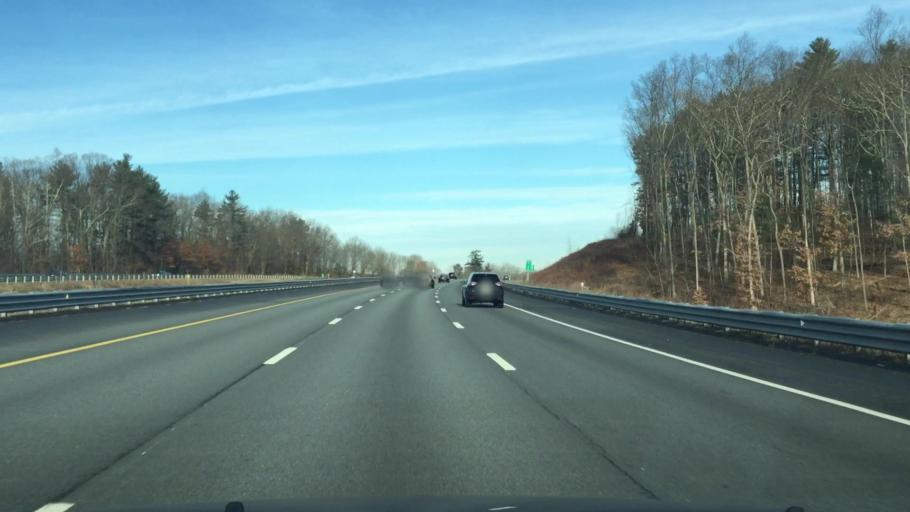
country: US
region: New Hampshire
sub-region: Rockingham County
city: Windham
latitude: 42.7909
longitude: -71.2702
